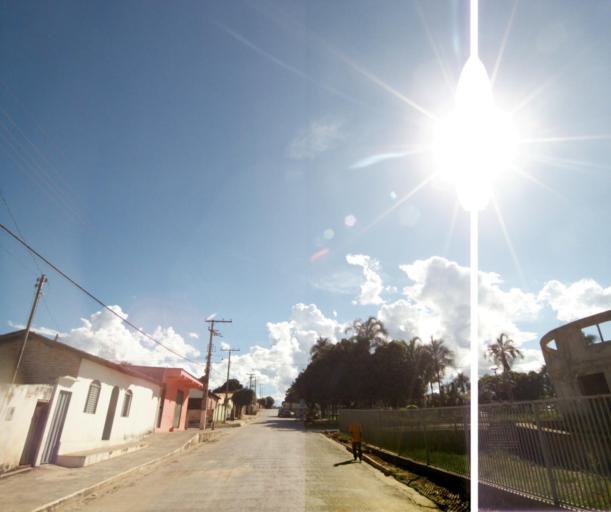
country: BR
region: Bahia
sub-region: Correntina
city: Correntina
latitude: -13.3460
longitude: -44.6375
